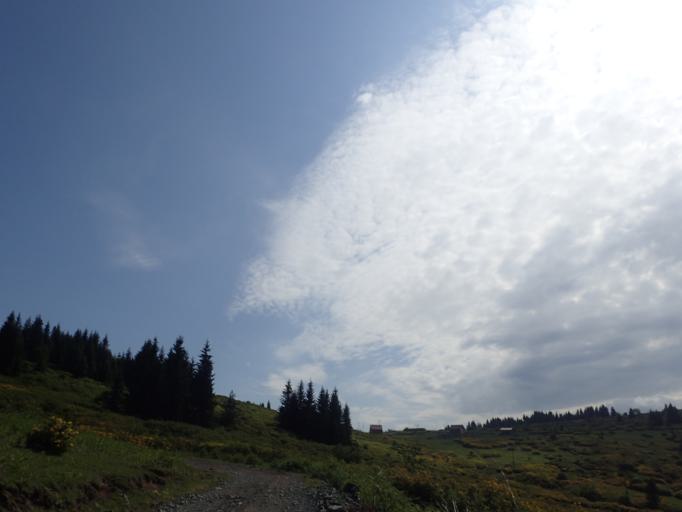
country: TR
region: Ordu
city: Topcam
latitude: 40.6890
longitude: 37.9428
